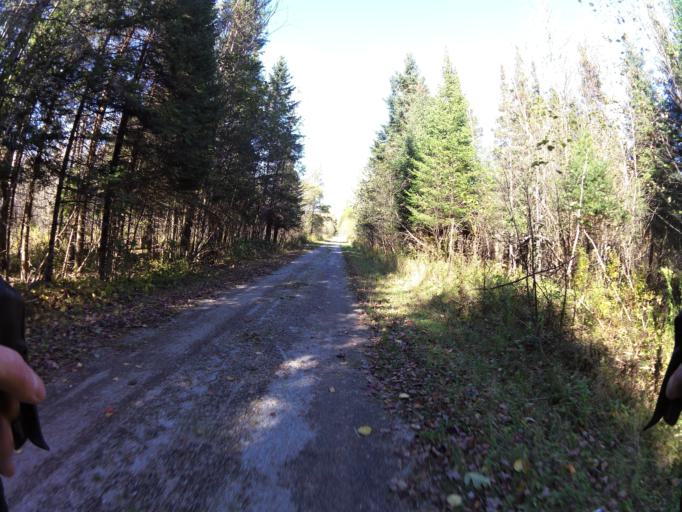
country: CA
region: Quebec
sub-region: Outaouais
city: Wakefield
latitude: 45.8867
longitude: -76.0321
